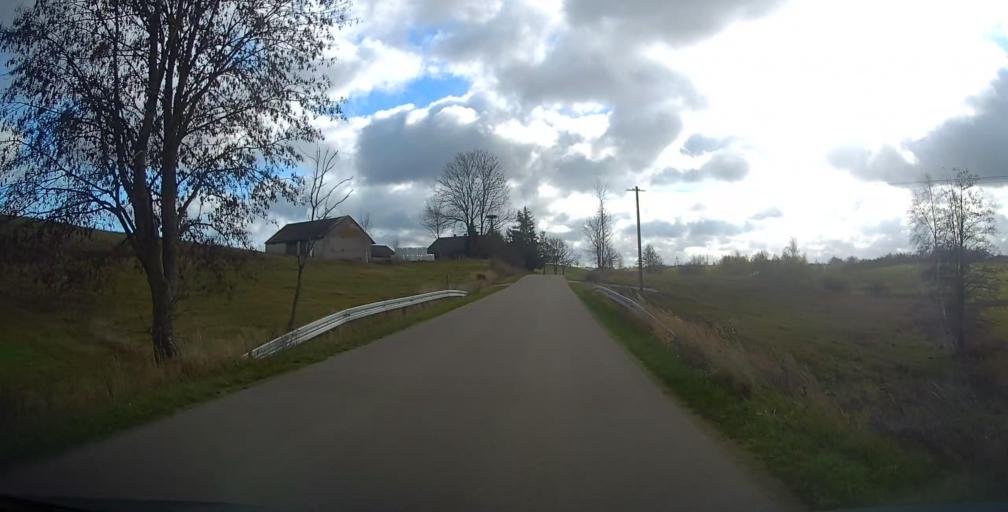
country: PL
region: Podlasie
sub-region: Suwalki
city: Suwalki
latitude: 54.3278
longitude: 22.8615
